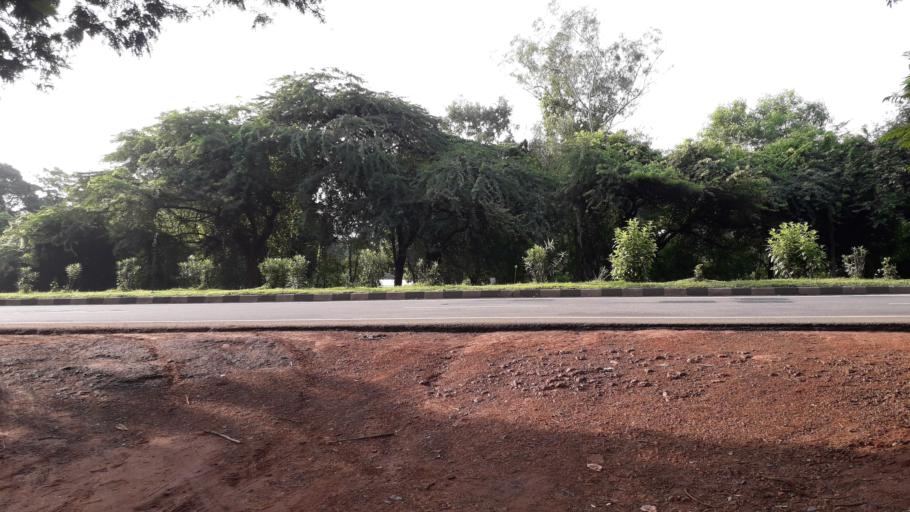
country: IN
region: Andhra Pradesh
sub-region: East Godavari
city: Rajahmundry
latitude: 17.0343
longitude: 81.8264
